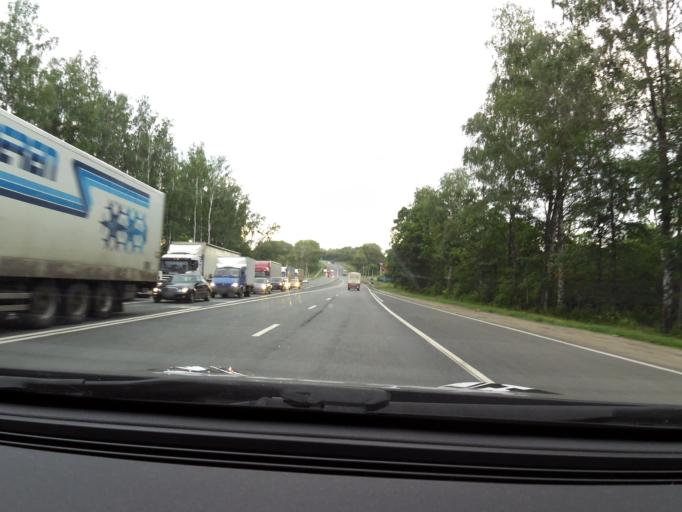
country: RU
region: Chuvashia
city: Tsivil'sk
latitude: 55.9027
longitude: 47.4291
